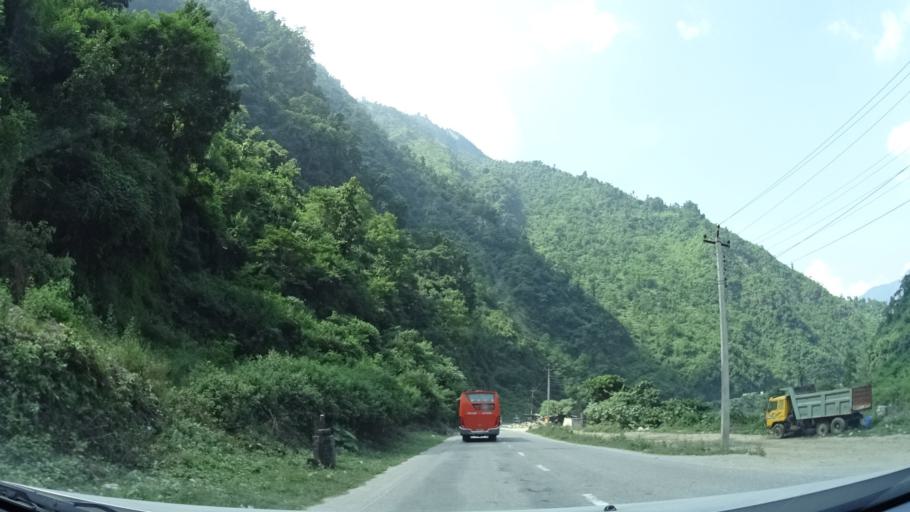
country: NP
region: Central Region
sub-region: Narayani Zone
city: Bharatpur
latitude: 27.8270
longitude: 84.6622
